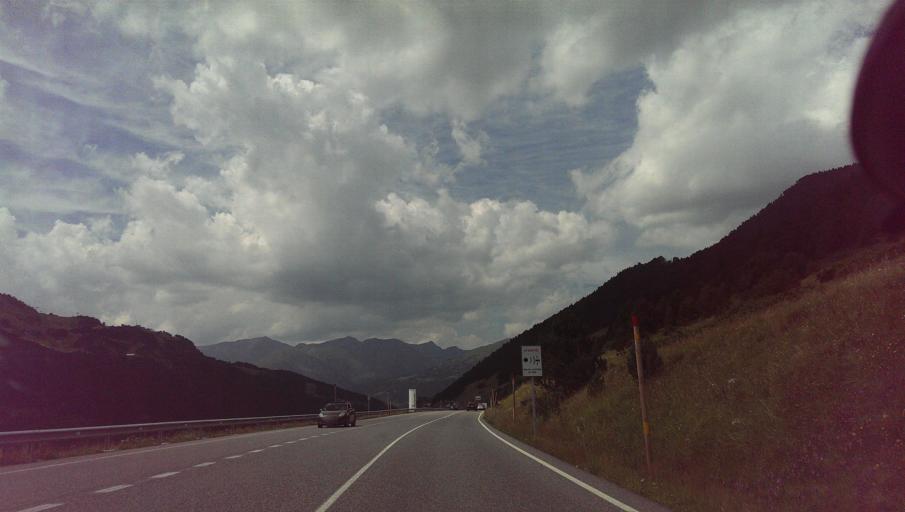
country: AD
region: Encamp
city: Pas de la Casa
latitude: 42.5539
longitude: 1.6921
